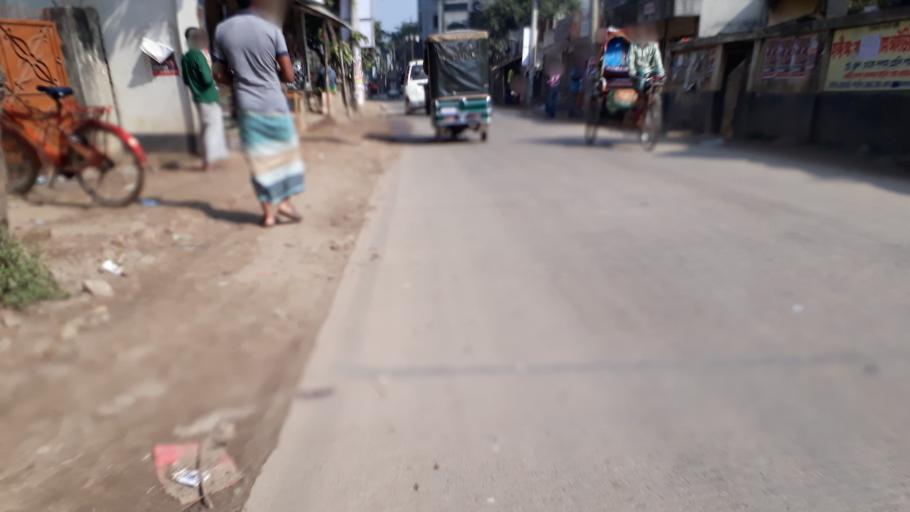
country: BD
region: Dhaka
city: Tungi
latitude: 23.8909
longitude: 90.3257
